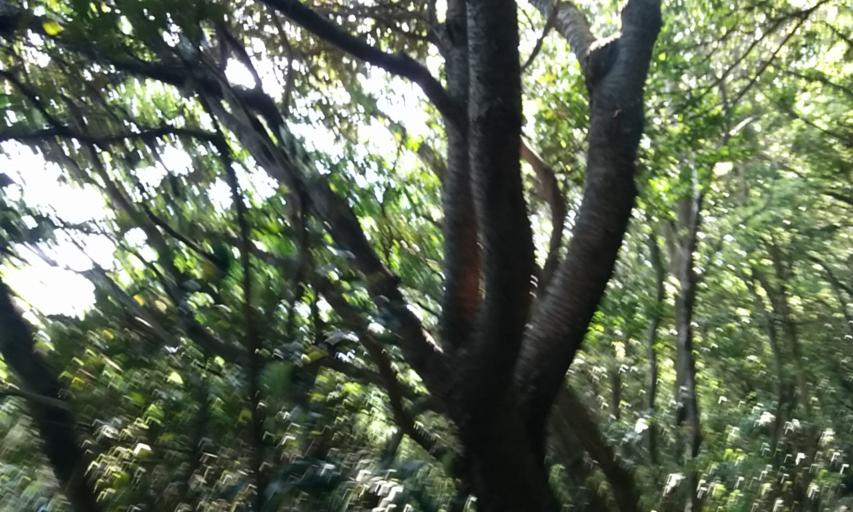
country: JP
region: Oita
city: Tsukumiura
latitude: 33.3468
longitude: 132.0192
